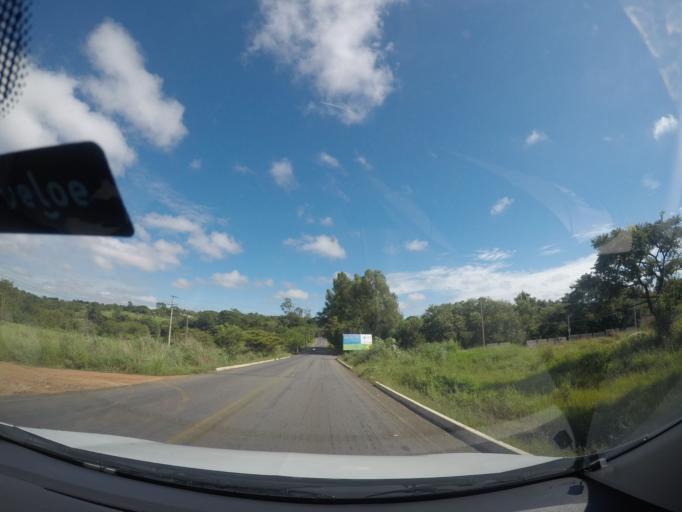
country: BR
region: Goias
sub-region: Senador Canedo
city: Senador Canedo
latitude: -16.6617
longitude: -49.1517
